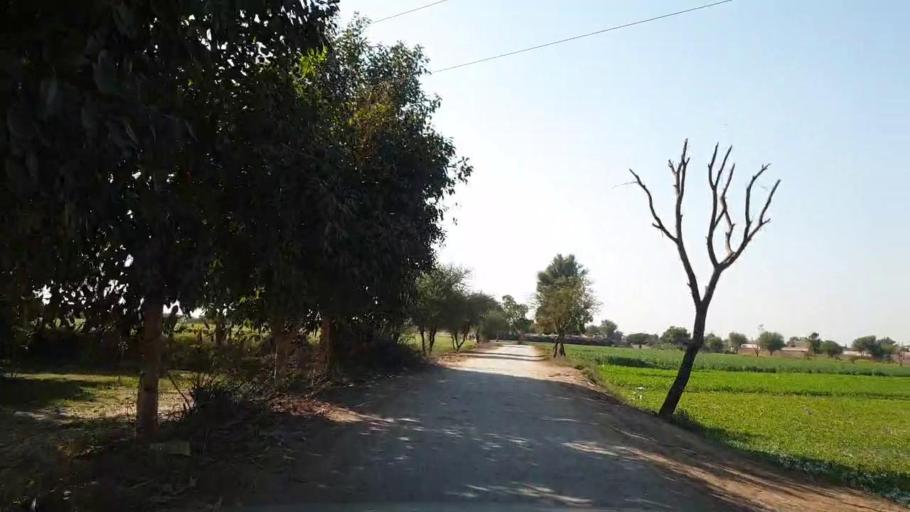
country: PK
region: Sindh
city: Tando Allahyar
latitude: 25.4824
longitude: 68.6818
